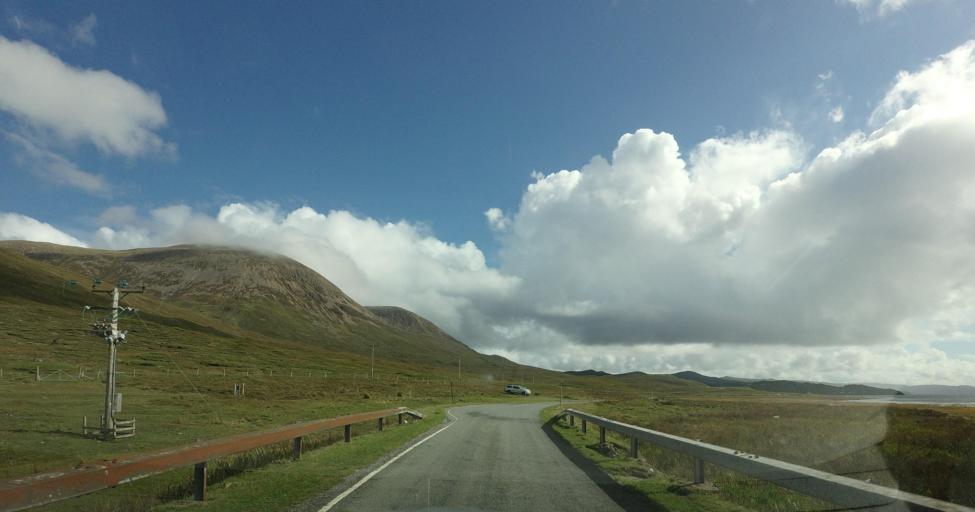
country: GB
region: Scotland
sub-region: Highland
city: Portree
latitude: 57.2279
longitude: -6.0368
